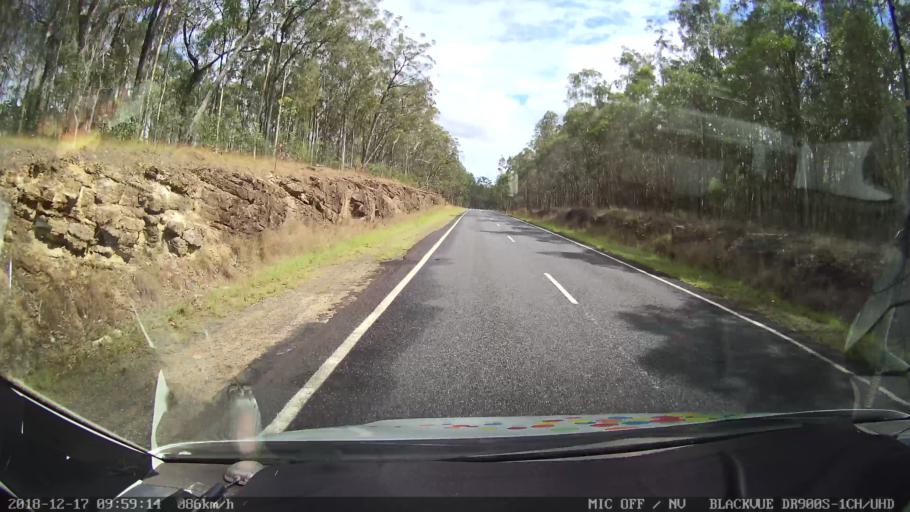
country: AU
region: New South Wales
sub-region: Tenterfield Municipality
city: Carrolls Creek
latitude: -28.9126
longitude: 152.4145
